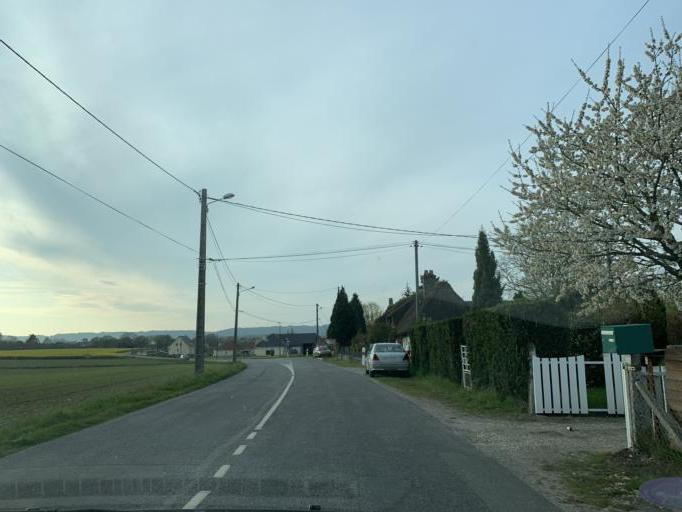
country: FR
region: Haute-Normandie
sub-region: Departement de la Seine-Maritime
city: Saint-Wandrille-Rancon
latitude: 49.5026
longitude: 0.7488
